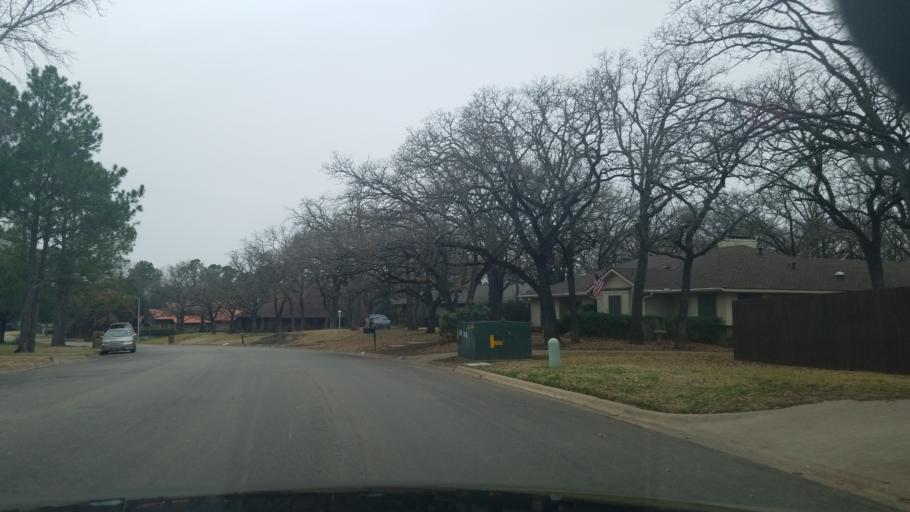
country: US
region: Texas
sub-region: Denton County
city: Denton
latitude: 33.1819
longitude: -97.1188
